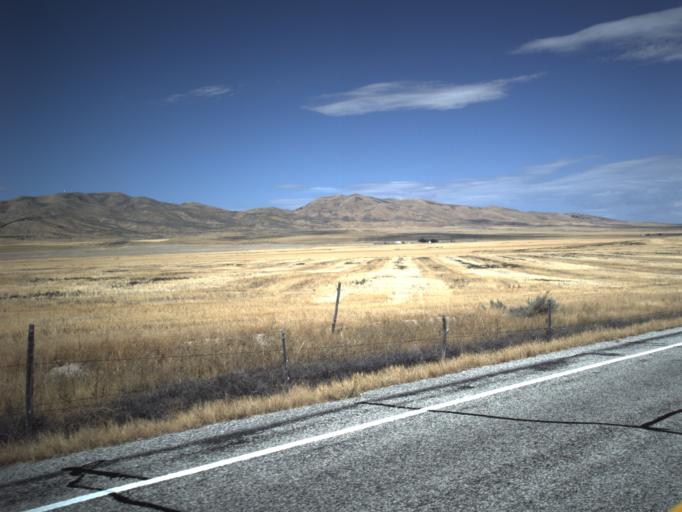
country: US
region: Utah
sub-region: Box Elder County
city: Tremonton
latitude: 41.7122
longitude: -112.4525
